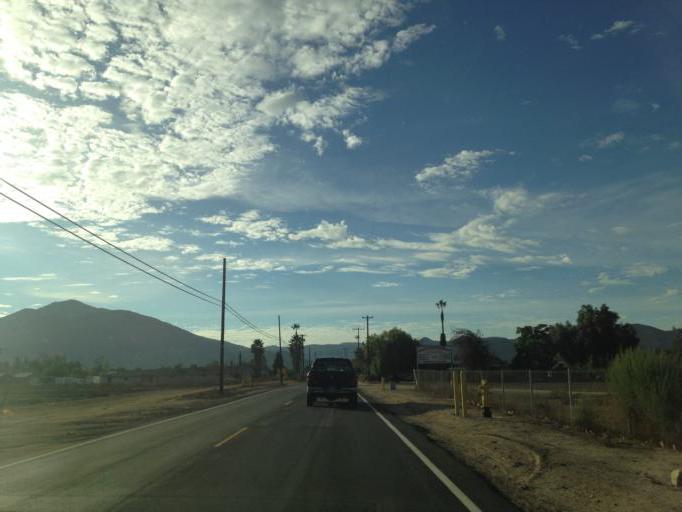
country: US
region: California
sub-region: San Diego County
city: Rainbow
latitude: 33.3726
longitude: -117.0787
